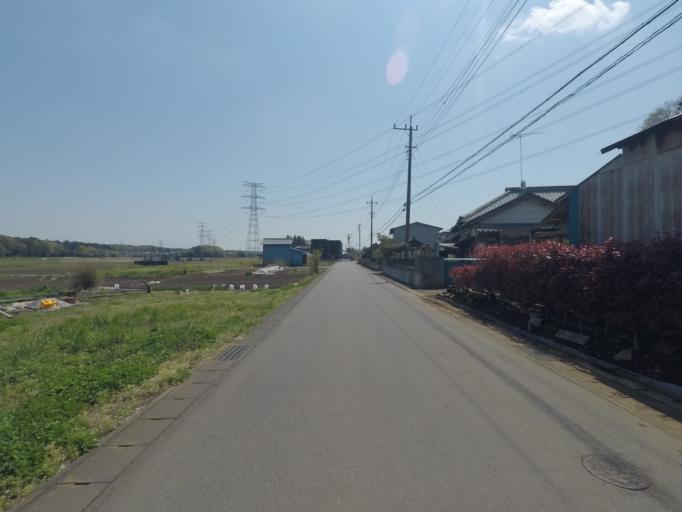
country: JP
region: Ibaraki
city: Ushiku
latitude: 36.0138
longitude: 140.0924
